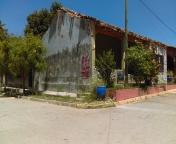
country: MX
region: Oaxaca
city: Asuncion Ixtaltepec
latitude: 16.5062
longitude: -95.0572
